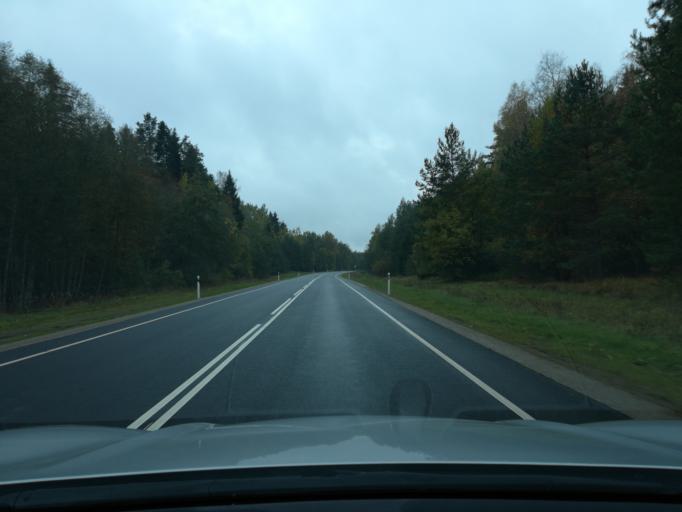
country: EE
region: Ida-Virumaa
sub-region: Johvi vald
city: Johvi
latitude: 59.1399
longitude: 27.3499
